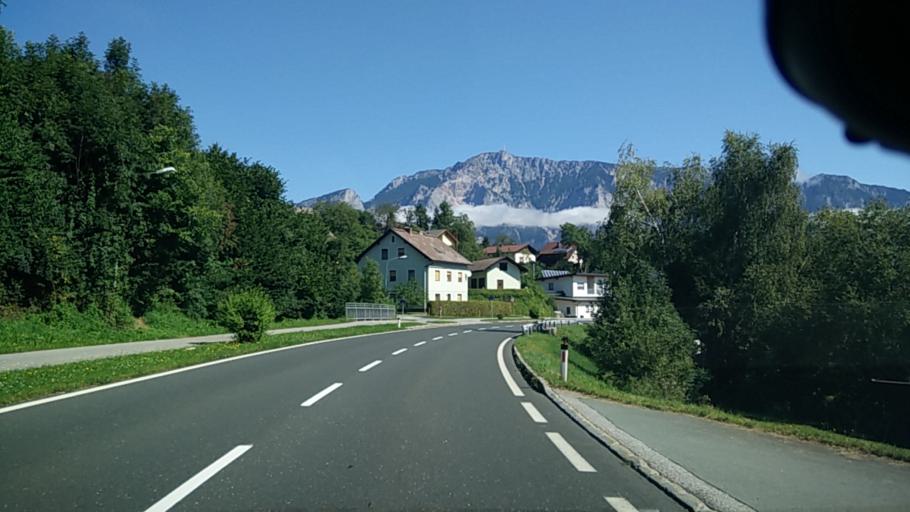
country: AT
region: Carinthia
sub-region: Politischer Bezirk Villach Land
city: Hohenthurn
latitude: 46.5405
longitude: 13.6448
